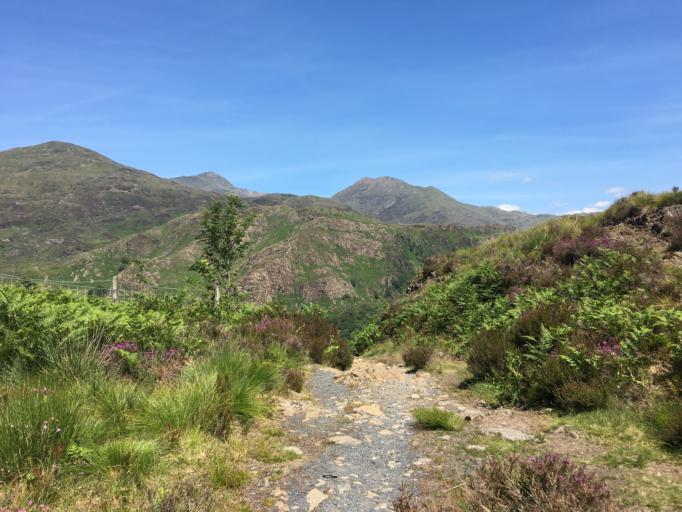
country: GB
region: Wales
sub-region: Gwynedd
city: Penrhyndeudraeth
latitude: 53.0184
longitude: -4.0708
